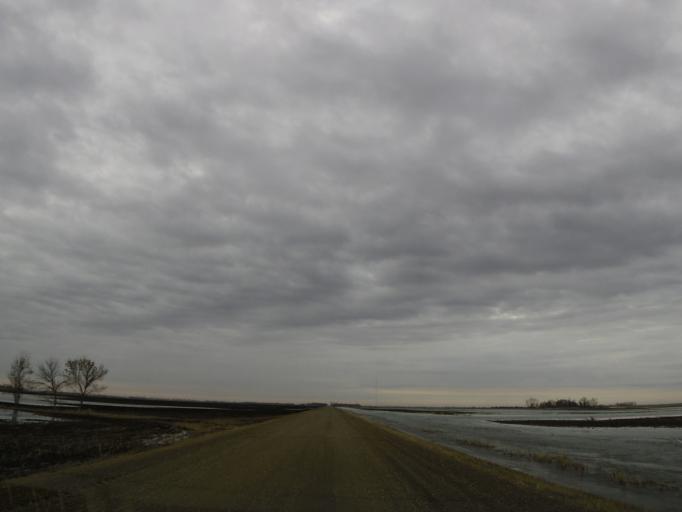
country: US
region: North Dakota
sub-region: Walsh County
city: Grafton
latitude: 48.4059
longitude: -97.4485
